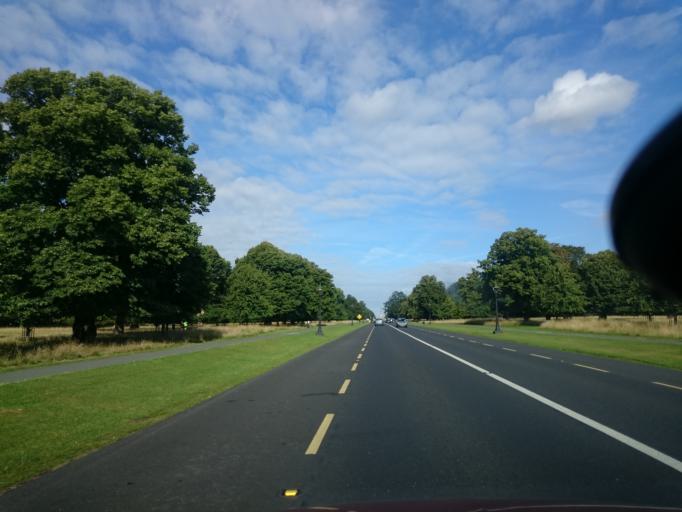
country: IE
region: Leinster
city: Chapelizod
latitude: 53.3581
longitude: -6.3211
